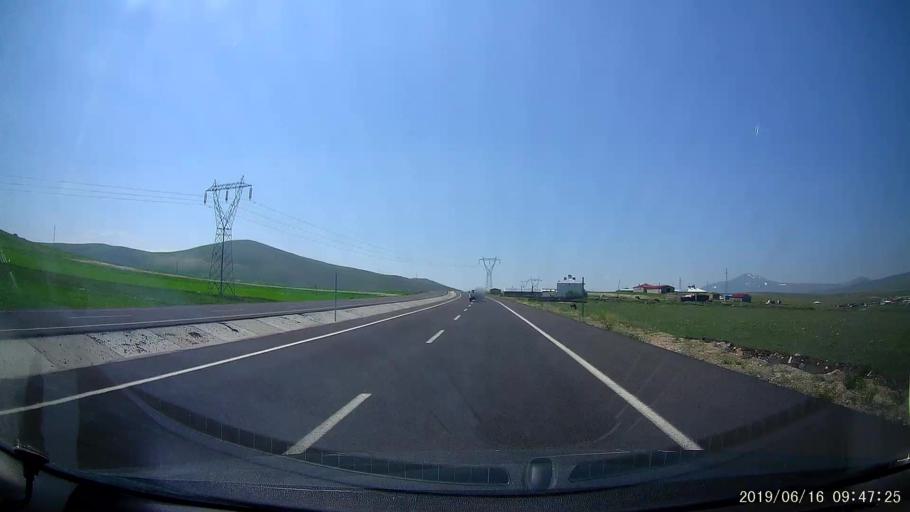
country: TR
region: Kars
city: Digor
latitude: 40.4479
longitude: 43.3433
